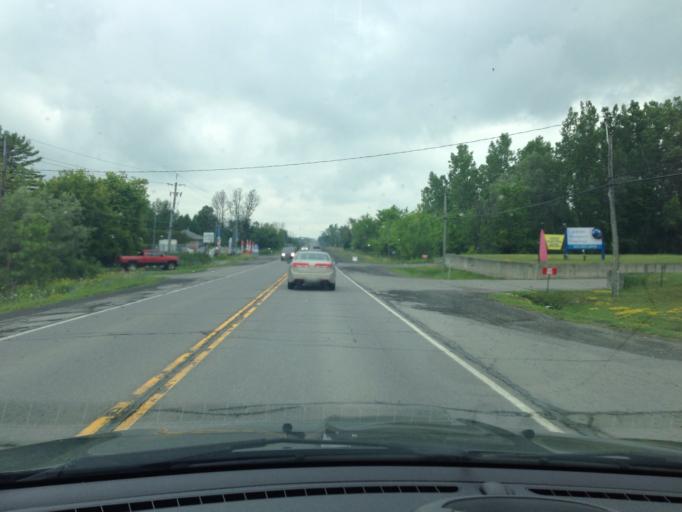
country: CA
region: Ontario
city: Ottawa
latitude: 45.3062
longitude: -75.5854
